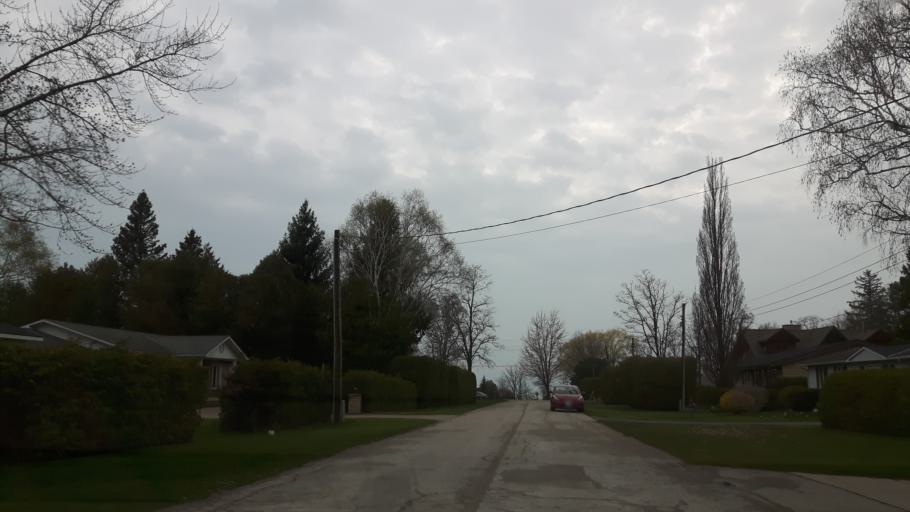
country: CA
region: Ontario
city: Bluewater
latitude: 43.5577
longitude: -81.7033
